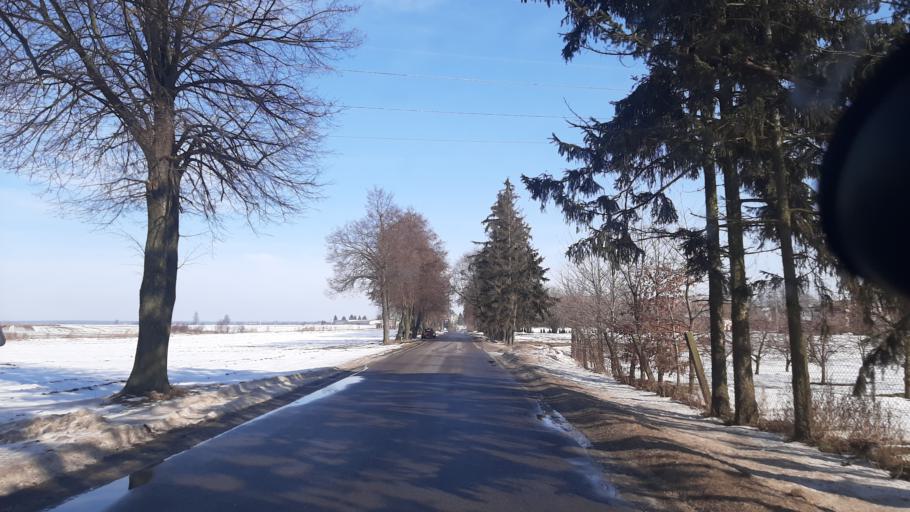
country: PL
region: Lublin Voivodeship
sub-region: Powiat pulawski
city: Kurow
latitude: 51.3803
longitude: 22.1598
